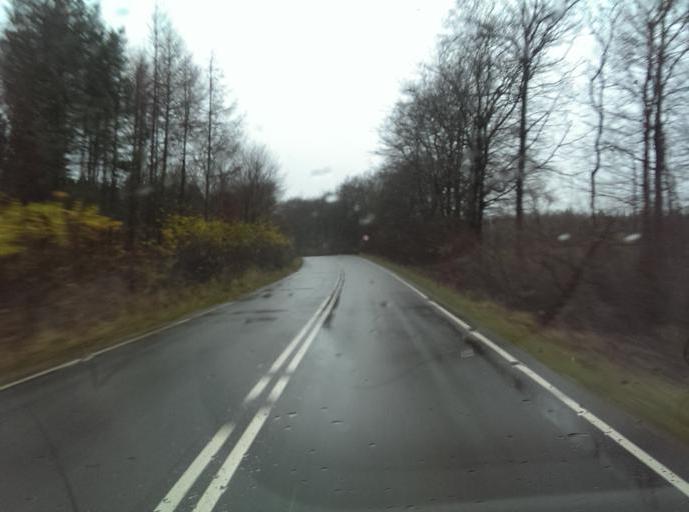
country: DK
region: South Denmark
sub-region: Esbjerg Kommune
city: Tjaereborg
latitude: 55.4823
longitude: 8.5795
